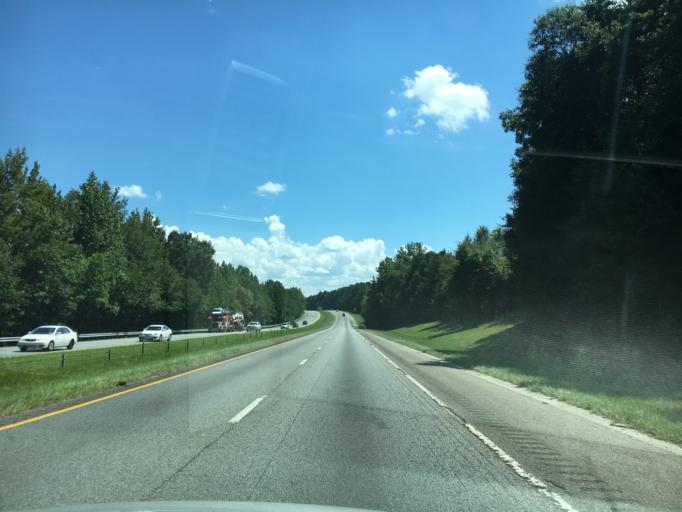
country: US
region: South Carolina
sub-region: Spartanburg County
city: Woodruff
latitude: 34.7429
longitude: -81.9545
